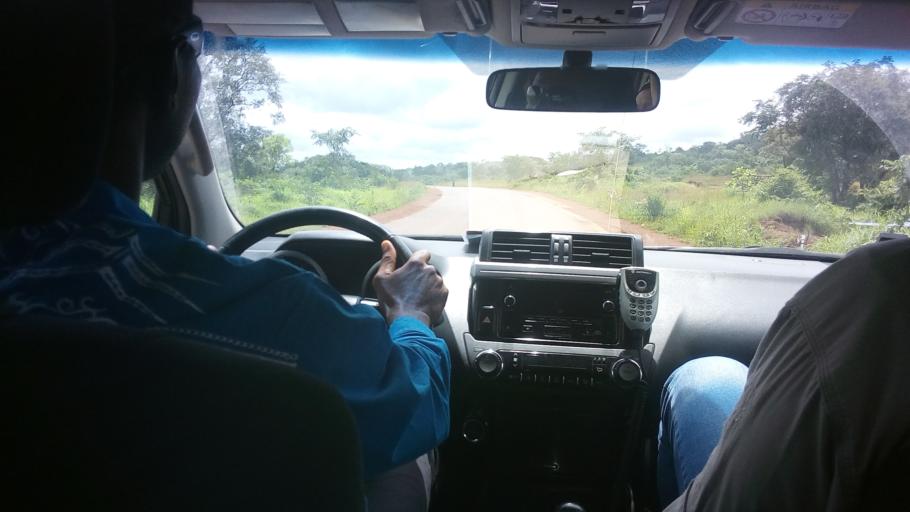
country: GN
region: Boke
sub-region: Boke Prefecture
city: Boke
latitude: 11.0233
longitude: -14.0670
